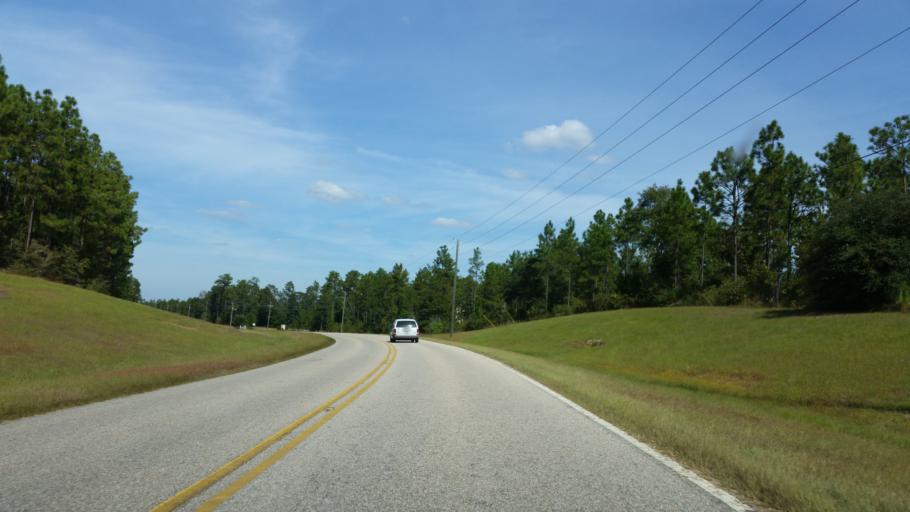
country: US
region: Alabama
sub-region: Baldwin County
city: Spanish Fort
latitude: 30.6889
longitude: -87.8462
